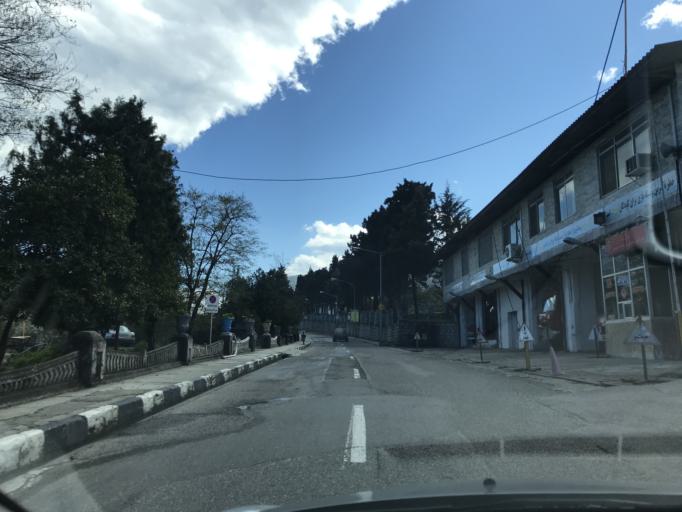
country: IR
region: Mazandaran
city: Ramsar
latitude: 36.9059
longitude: 50.6536
